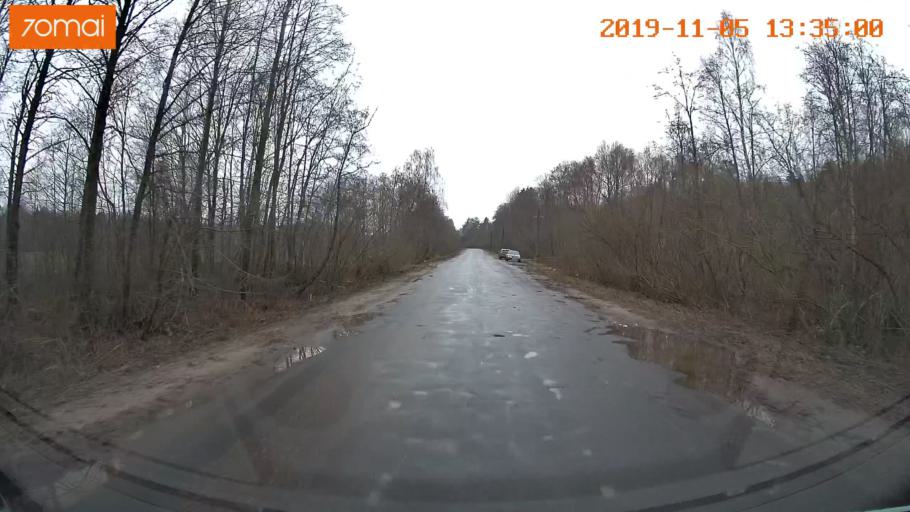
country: RU
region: Ivanovo
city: Shuya
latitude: 56.9048
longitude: 41.3891
